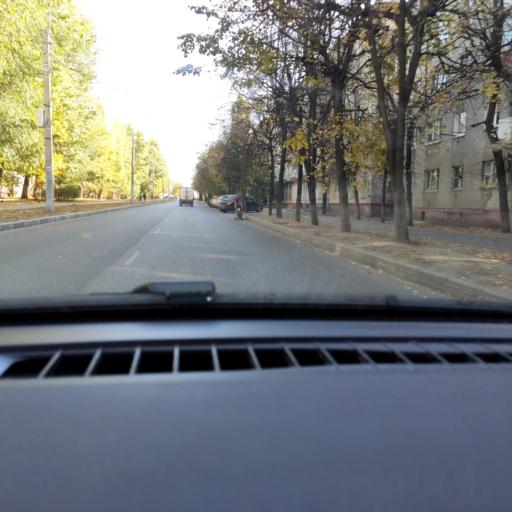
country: RU
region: Voronezj
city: Voronezh
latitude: 51.6563
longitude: 39.1464
